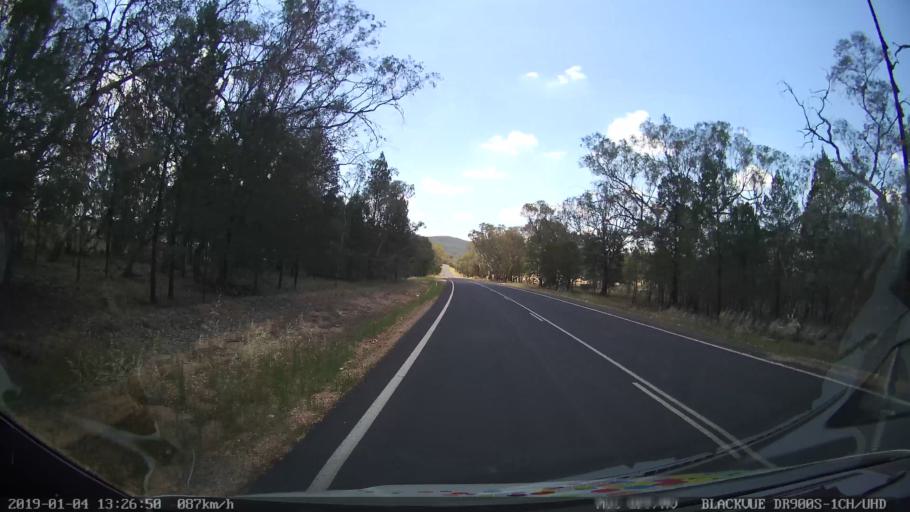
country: AU
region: New South Wales
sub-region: Parkes
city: Peak Hill
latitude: -32.6766
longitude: 148.5602
